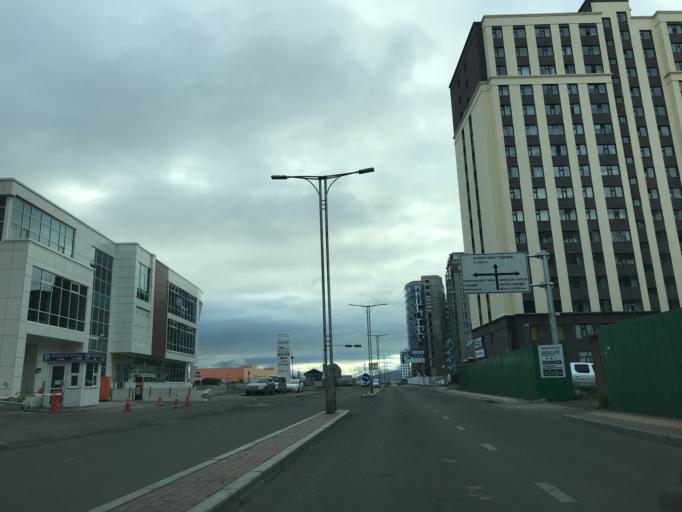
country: MN
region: Ulaanbaatar
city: Ulaanbaatar
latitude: 47.9048
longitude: 106.9418
